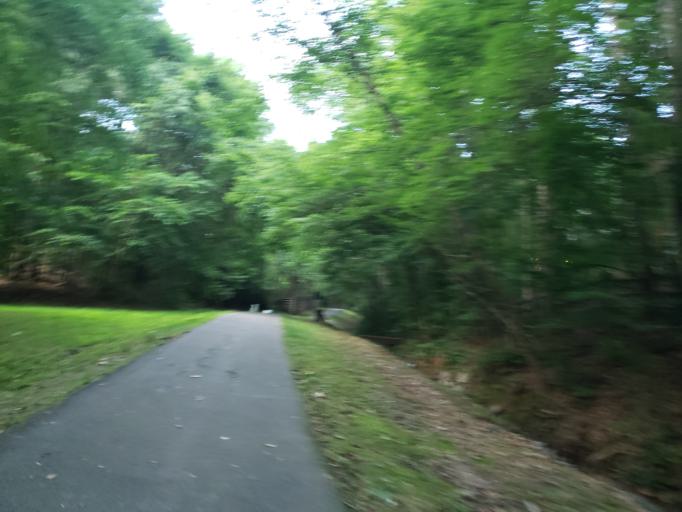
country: US
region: North Carolina
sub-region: Durham County
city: Durham
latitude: 35.9199
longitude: -78.9374
